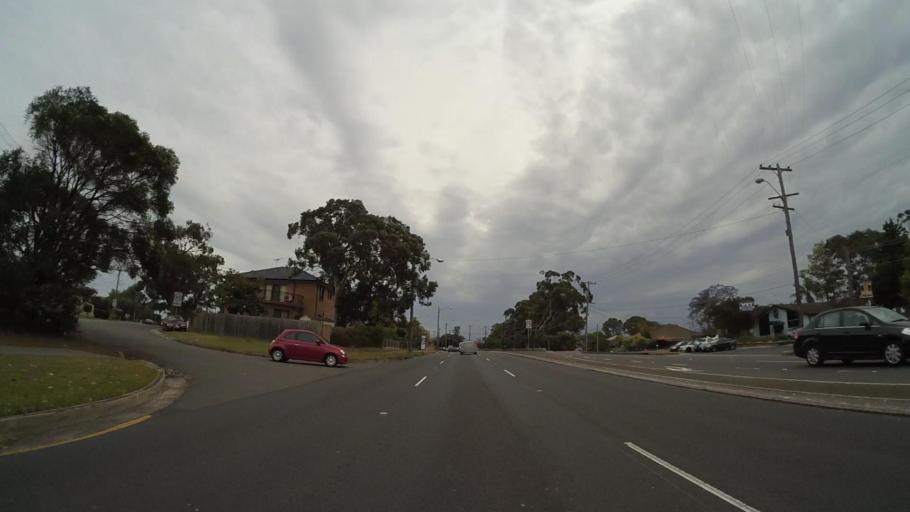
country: AU
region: New South Wales
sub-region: Sutherland Shire
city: Kareela
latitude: -34.0171
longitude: 151.0921
